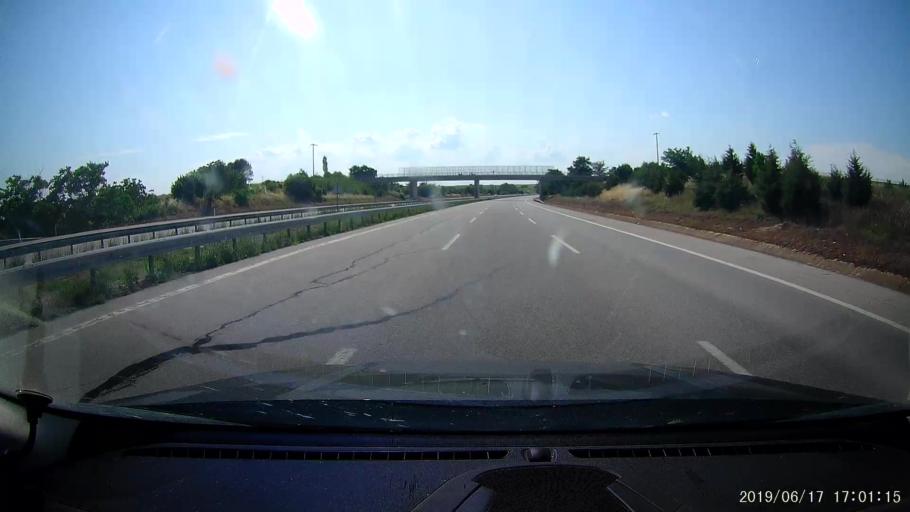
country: TR
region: Edirne
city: Haskoy
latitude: 41.6274
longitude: 26.8092
